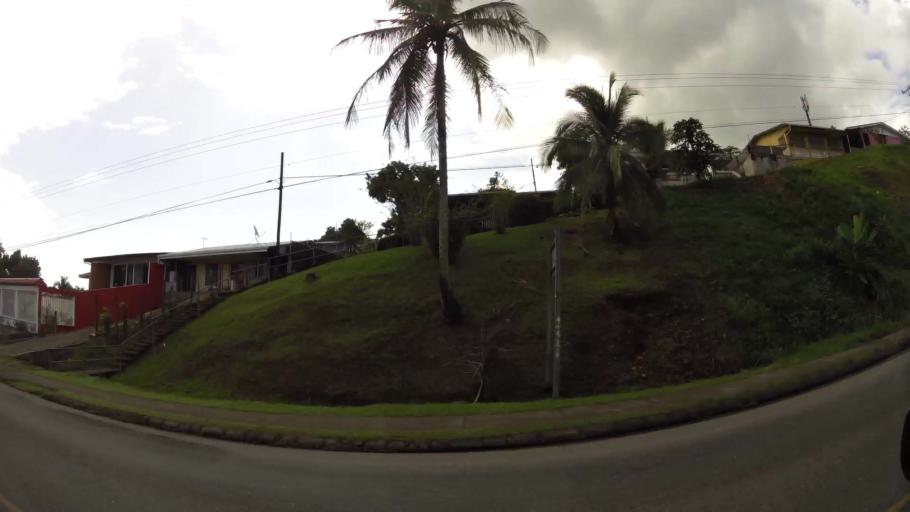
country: CR
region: Limon
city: Limon
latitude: 9.9852
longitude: -83.0554
